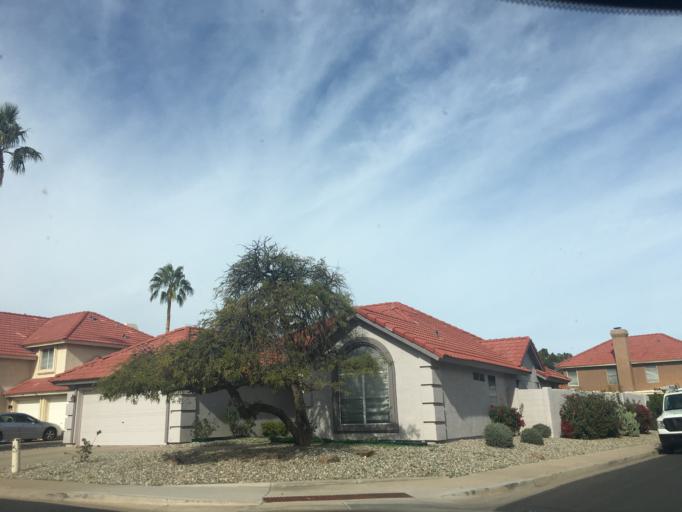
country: US
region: Arizona
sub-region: Maricopa County
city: Gilbert
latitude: 33.3443
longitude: -111.8055
